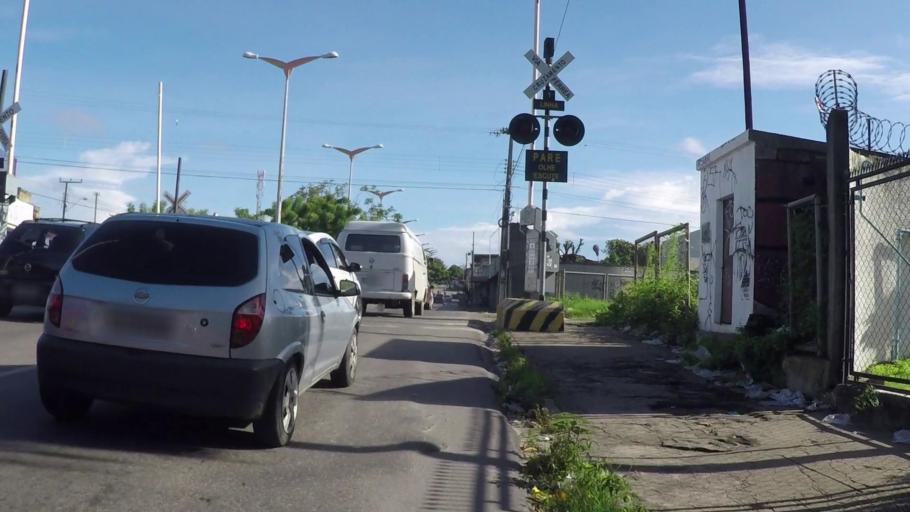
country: BR
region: Ceara
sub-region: Fortaleza
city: Fortaleza
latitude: -3.7317
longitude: -38.5845
